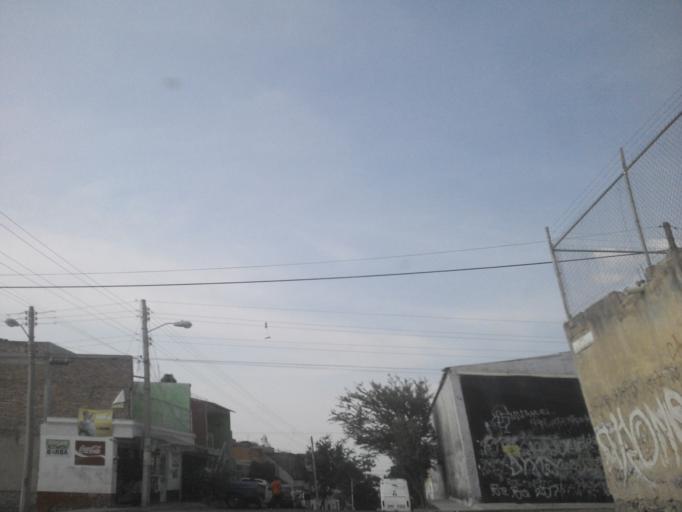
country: MX
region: Jalisco
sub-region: Tlajomulco de Zuniga
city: Altus Bosques
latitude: 20.6073
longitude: -103.3783
